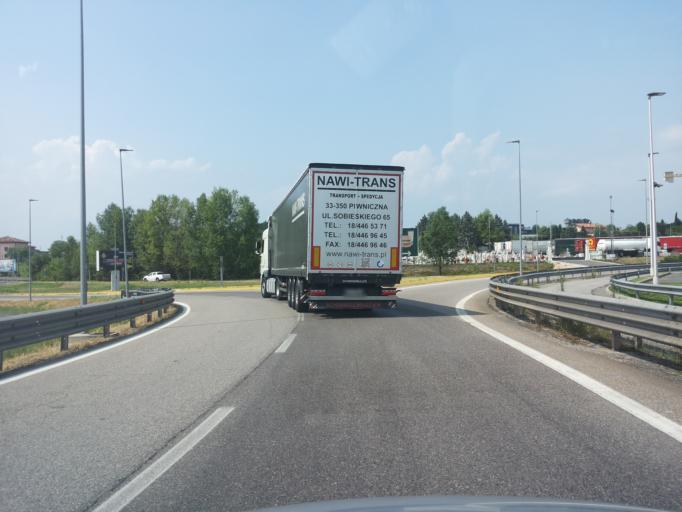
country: IT
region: Veneto
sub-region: Provincia di Verona
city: Cavalcaselle
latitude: 45.4319
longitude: 10.7073
